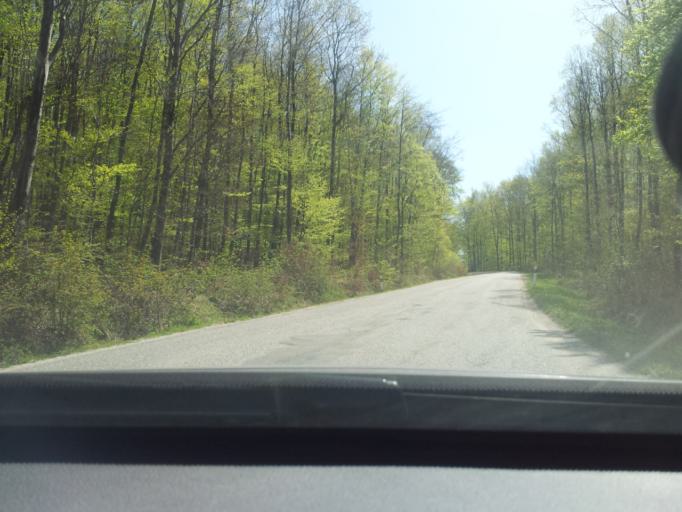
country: SK
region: Nitriansky
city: Partizanske
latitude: 48.5134
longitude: 18.3972
